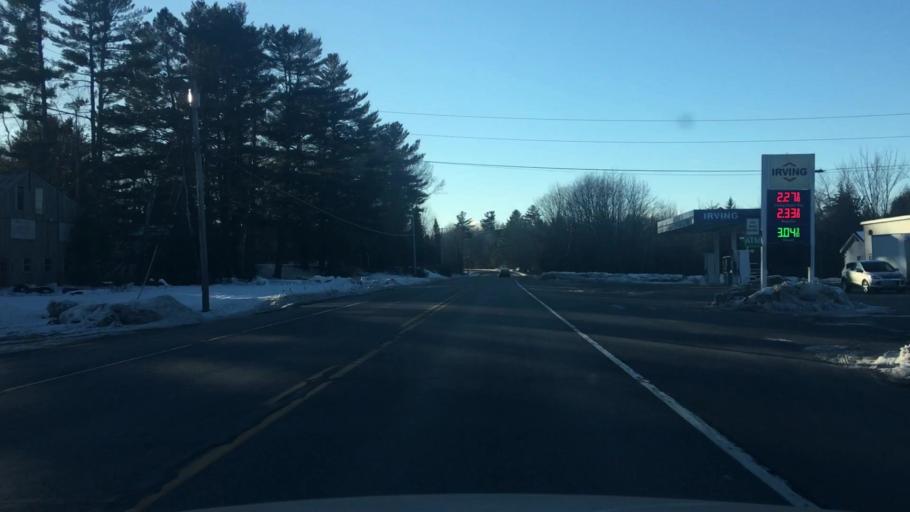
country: US
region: Maine
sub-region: Franklin County
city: New Sharon
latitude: 44.6777
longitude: -69.9226
